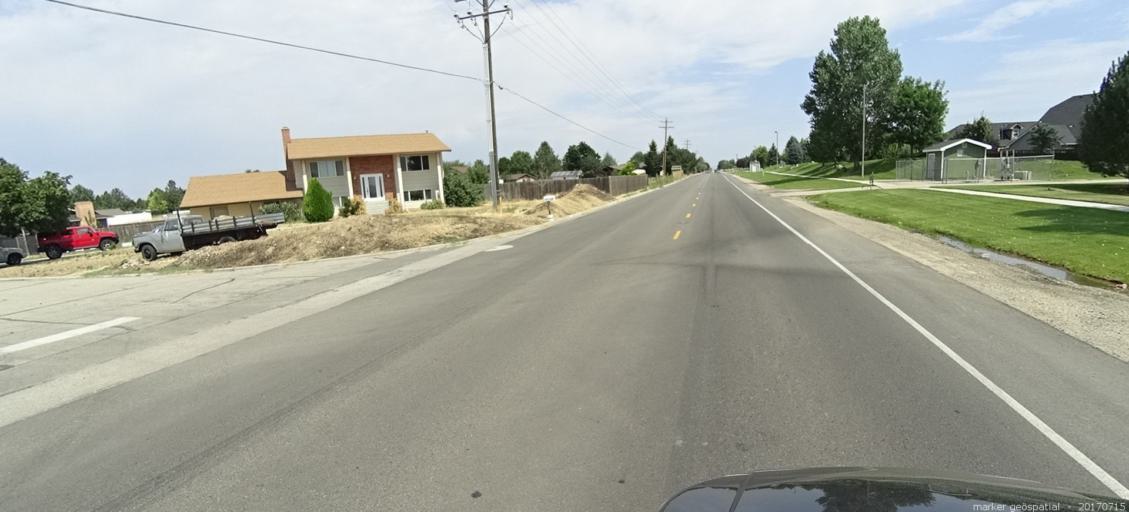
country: US
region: Idaho
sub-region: Ada County
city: Garden City
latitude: 43.5464
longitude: -116.2742
